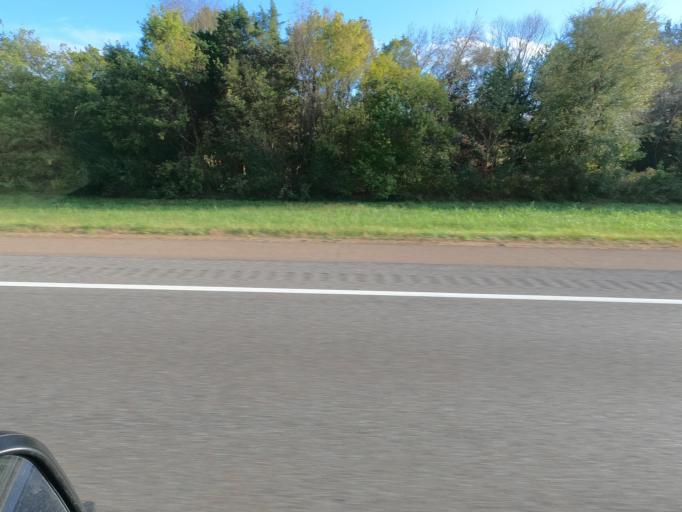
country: US
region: Tennessee
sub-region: Henderson County
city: Lexington
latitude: 35.7703
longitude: -88.4487
